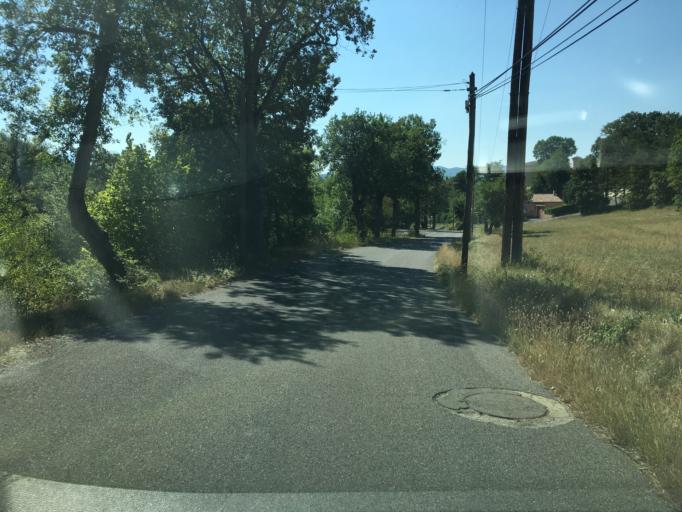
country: FR
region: Provence-Alpes-Cote d'Azur
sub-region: Departement des Alpes-de-Haute-Provence
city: Mallemoisson
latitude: 44.0619
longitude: 6.1479
